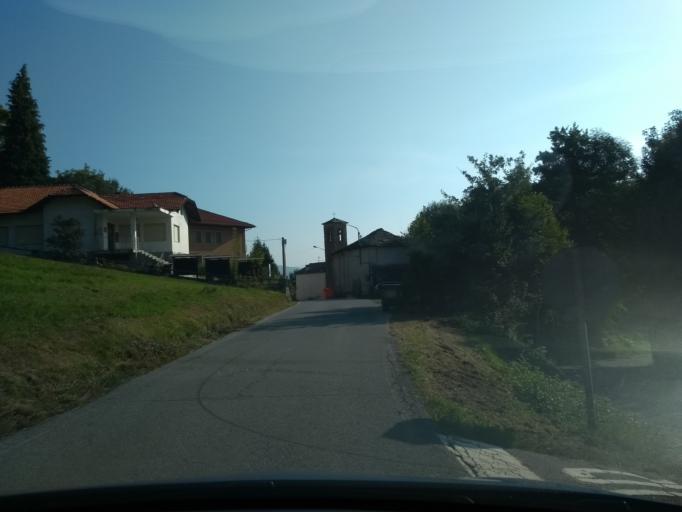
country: IT
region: Piedmont
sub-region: Provincia di Torino
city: Corio
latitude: 45.3024
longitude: 7.5041
